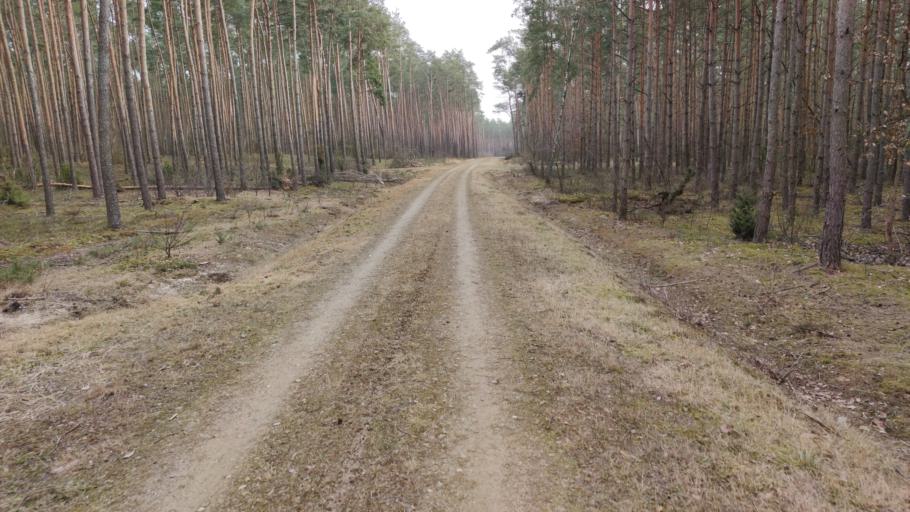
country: PL
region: Masovian Voivodeship
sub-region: Powiat plocki
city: Bodzanow
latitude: 52.4517
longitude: 19.9623
